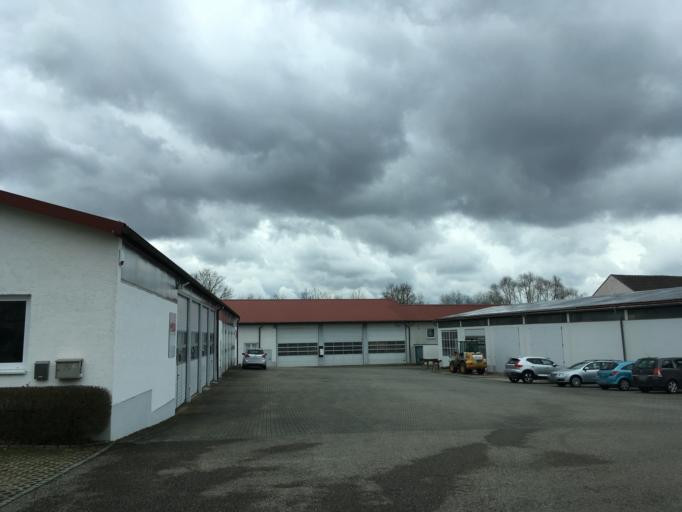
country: DE
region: Bavaria
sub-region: Upper Bavaria
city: Markt Schwaben
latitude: 48.1757
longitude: 11.8611
